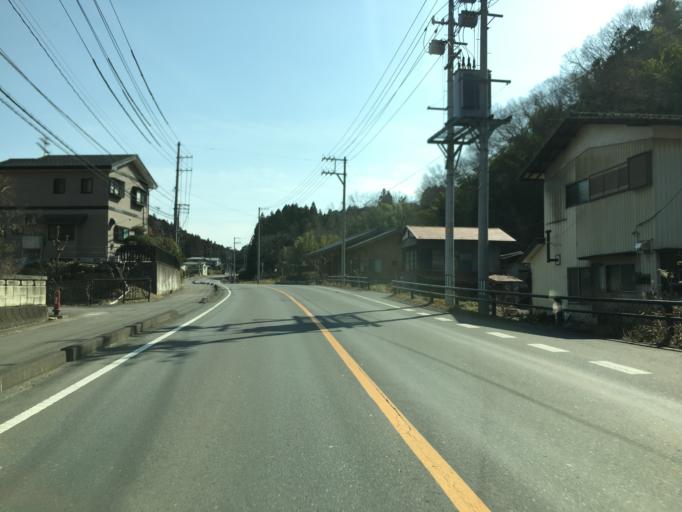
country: JP
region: Ibaraki
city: Daigo
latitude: 36.8602
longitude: 140.4280
